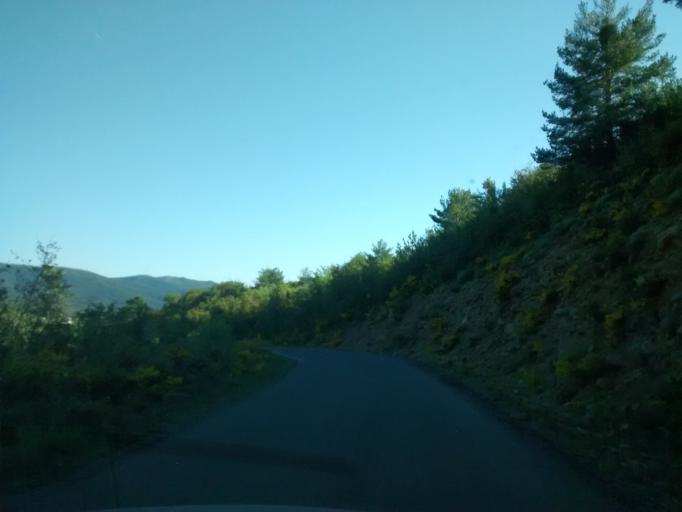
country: ES
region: Aragon
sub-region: Provincia de Huesca
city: Jasa
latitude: 42.6932
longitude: -0.6214
